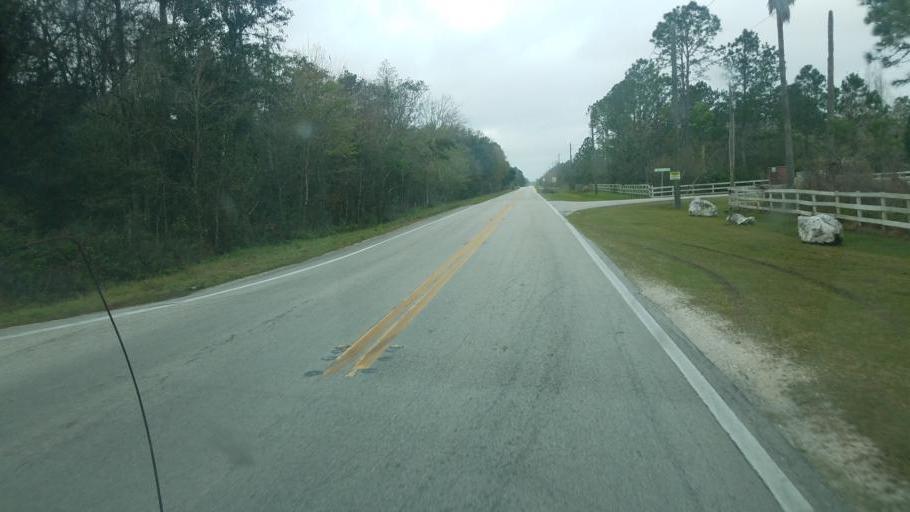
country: US
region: Florida
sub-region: Polk County
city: Polk City
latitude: 28.2586
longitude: -81.9224
